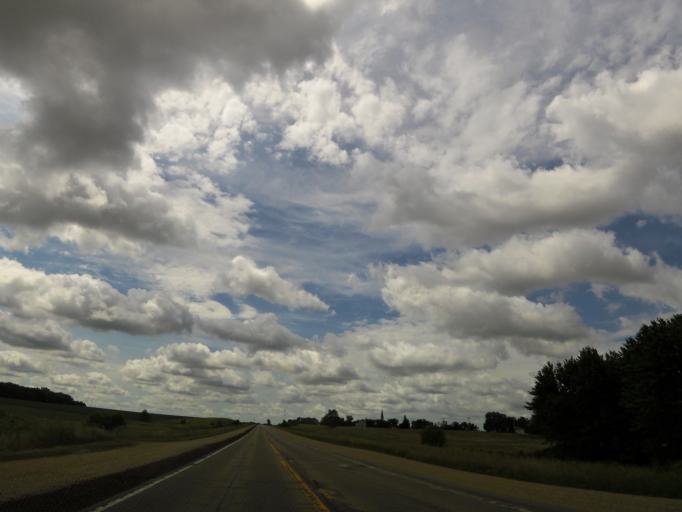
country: US
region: Iowa
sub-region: Chickasaw County
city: New Hampton
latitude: 43.2691
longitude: -92.2979
